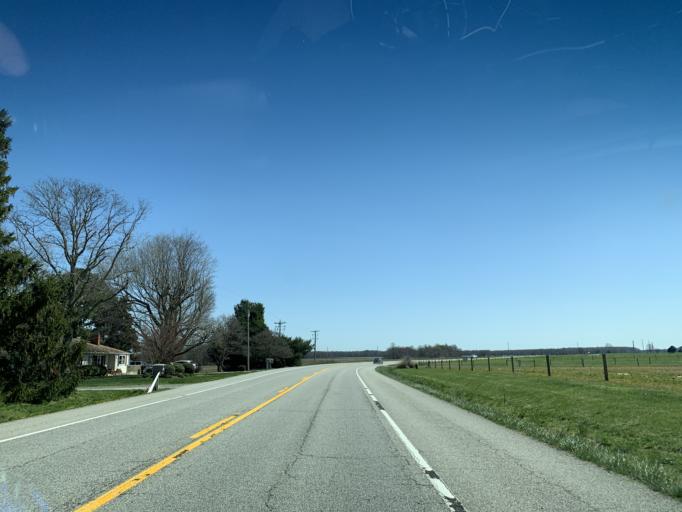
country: US
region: Maryland
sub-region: Queen Anne's County
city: Centreville
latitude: 39.0011
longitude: -76.0602
